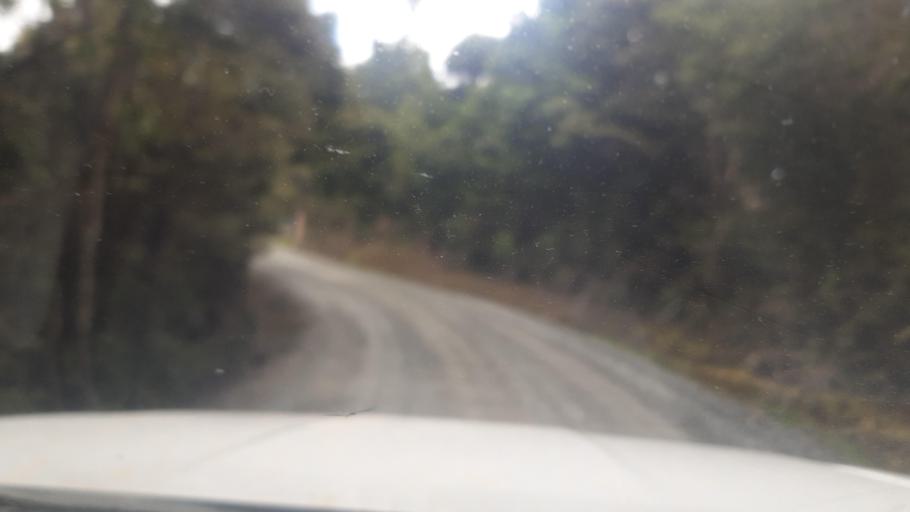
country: NZ
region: Northland
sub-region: Far North District
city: Taipa
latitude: -35.0723
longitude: 173.5252
